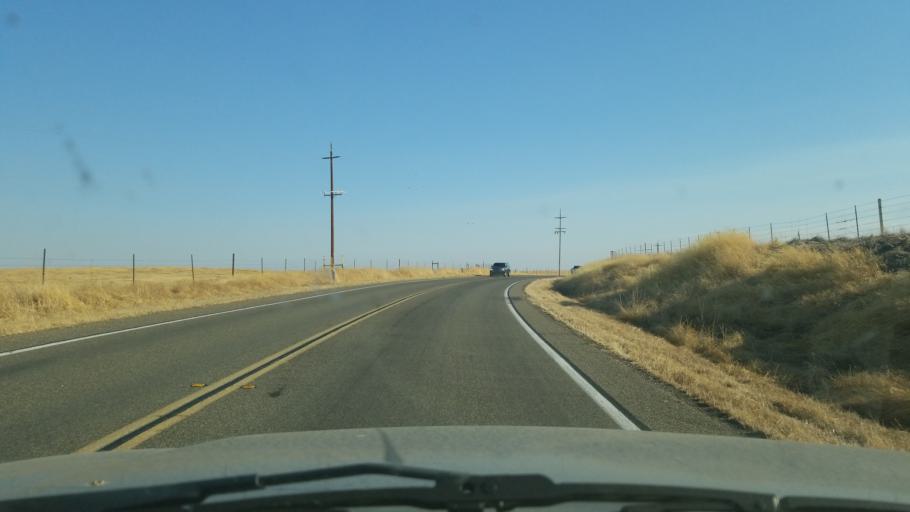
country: US
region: California
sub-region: Merced County
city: Merced
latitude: 37.4469
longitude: -120.4303
